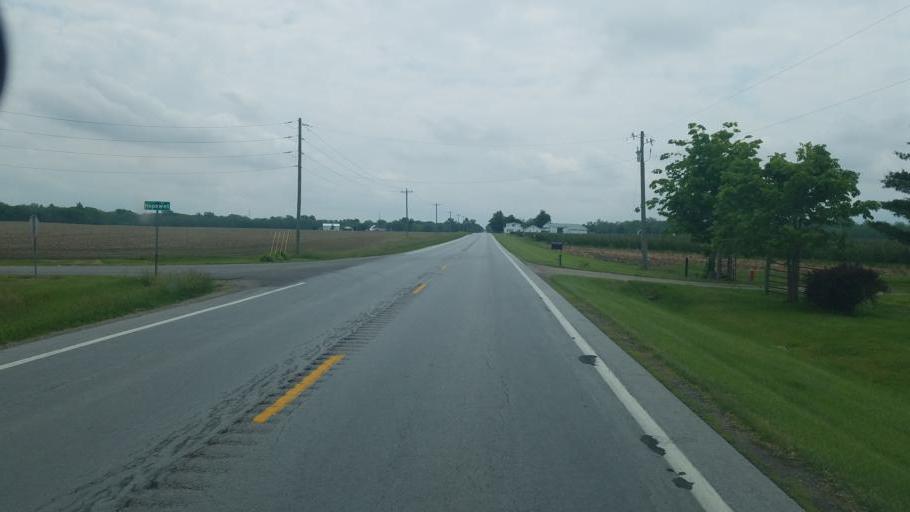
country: US
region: Ohio
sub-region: Union County
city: Richwood
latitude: 40.3565
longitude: -83.2980
